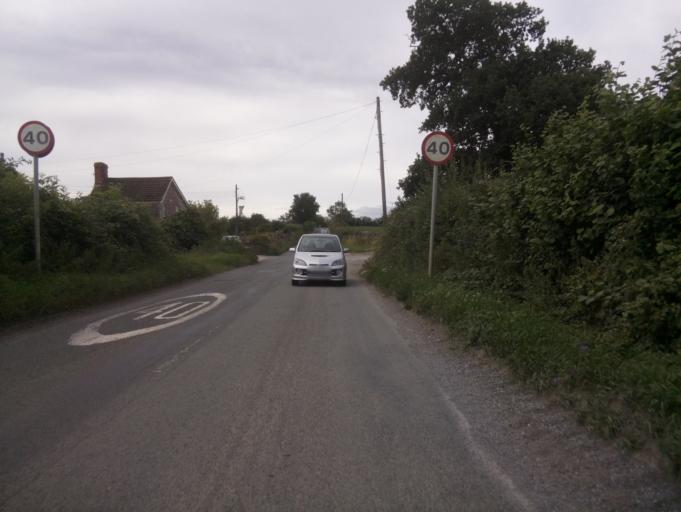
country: GB
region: England
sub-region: Somerset
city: Street
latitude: 51.1084
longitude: -2.6986
